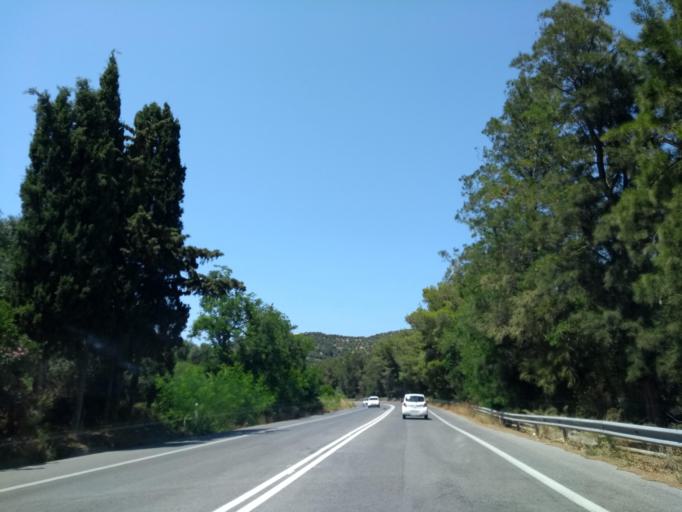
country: GR
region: Crete
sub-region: Nomos Rethymnis
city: Anogeia
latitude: 35.3961
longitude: 24.8784
